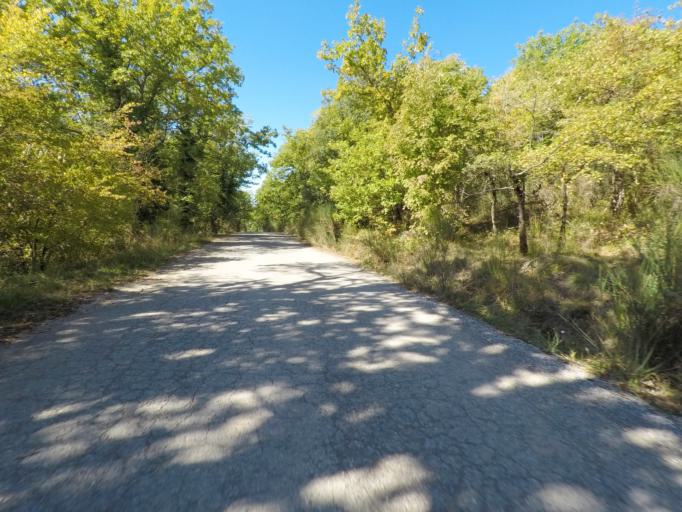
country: IT
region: Tuscany
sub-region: Provincia di Siena
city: Castellina in Chianti
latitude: 43.4370
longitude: 11.3267
